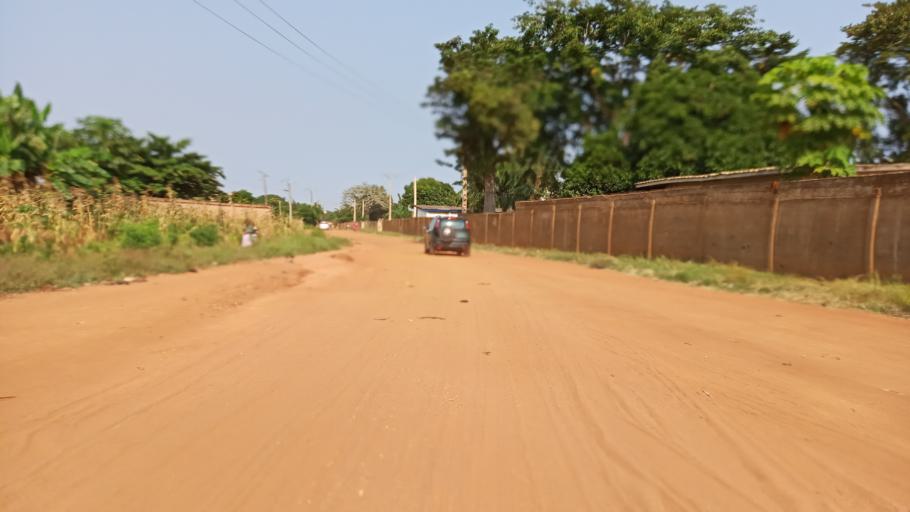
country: TG
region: Maritime
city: Lome
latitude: 6.2088
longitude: 1.2005
